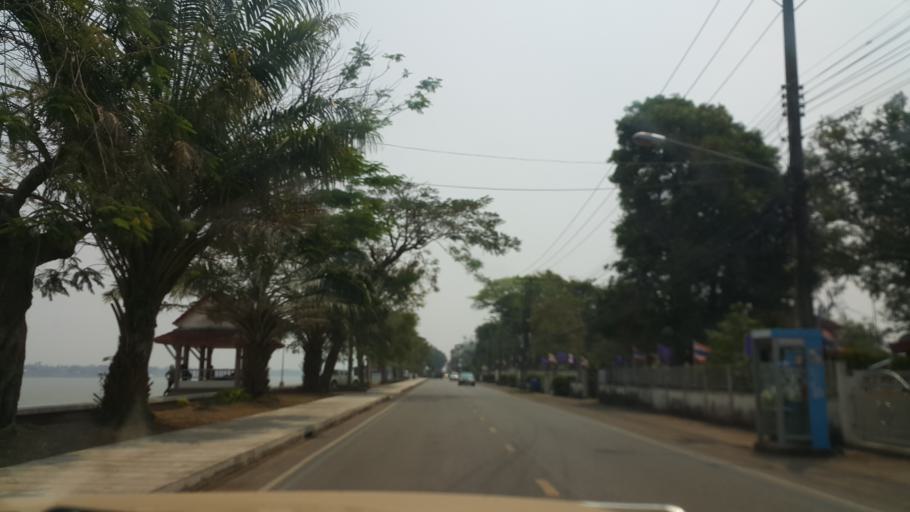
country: TH
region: Nakhon Phanom
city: Nakhon Phanom
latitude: 17.4072
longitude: 104.7859
